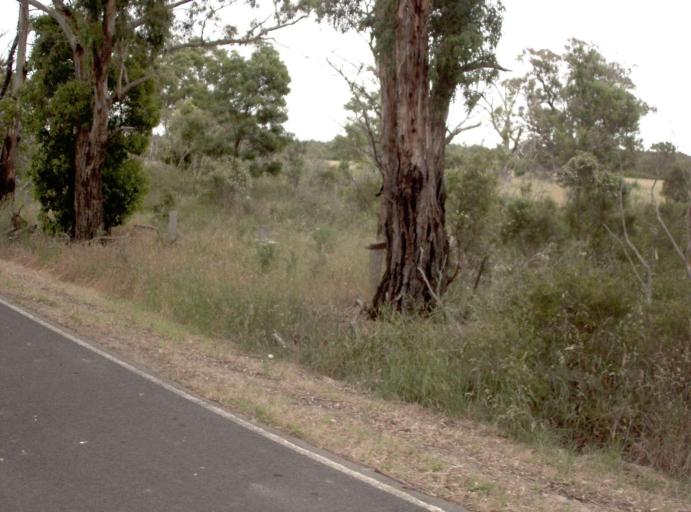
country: AU
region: Victoria
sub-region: Latrobe
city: Traralgon
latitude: -38.4871
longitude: 146.8199
